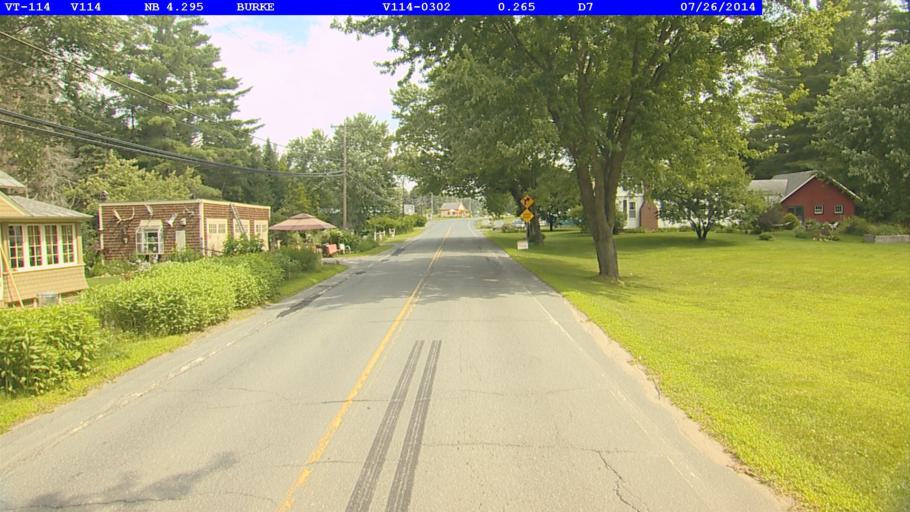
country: US
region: Vermont
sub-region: Caledonia County
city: Lyndonville
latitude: 44.5862
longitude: -71.9473
